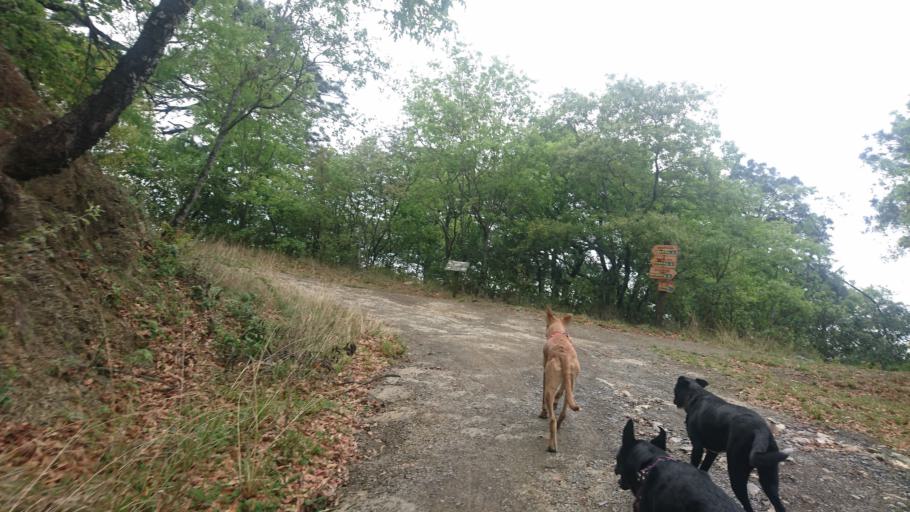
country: MX
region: Nuevo Leon
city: Garza Garcia
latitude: 25.6063
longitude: -100.3414
